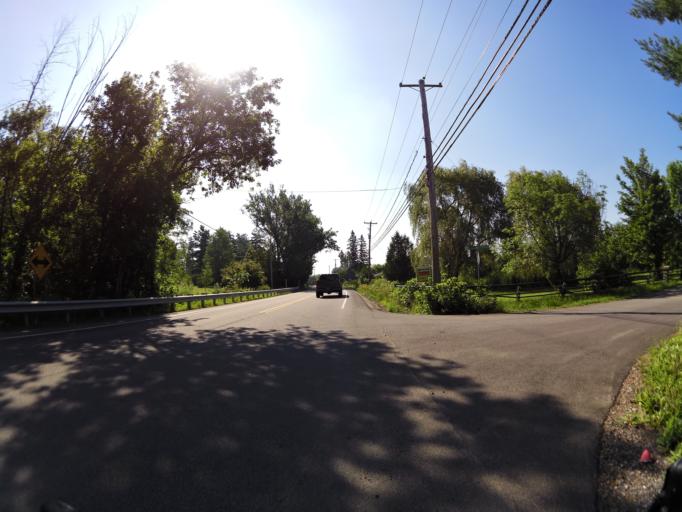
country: CA
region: Quebec
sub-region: Outaouais
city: Gatineau
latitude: 45.4920
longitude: -75.7687
